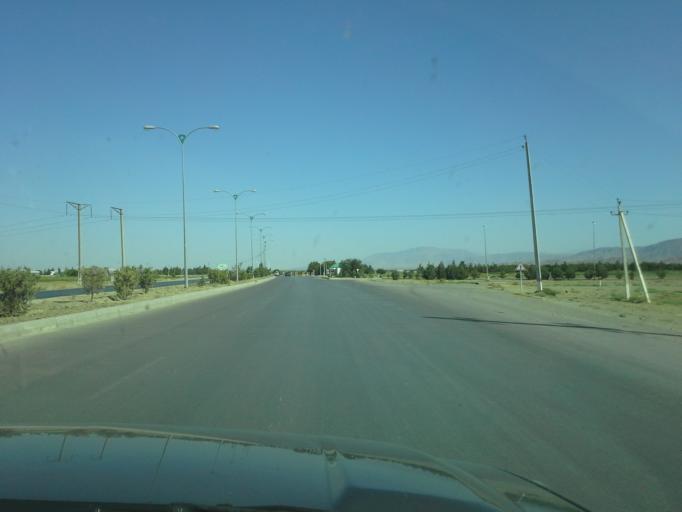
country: TM
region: Ahal
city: Baharly
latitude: 38.4195
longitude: 57.4417
